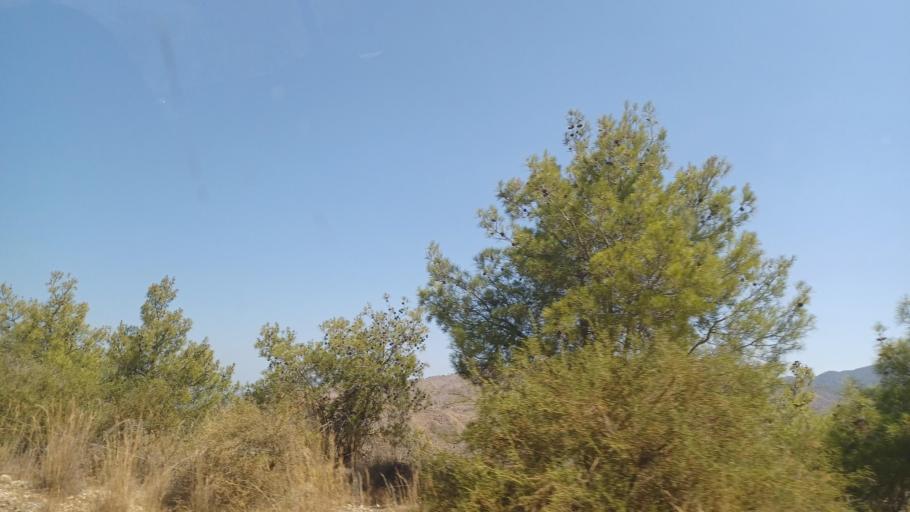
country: CY
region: Pafos
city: Polis
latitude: 35.0399
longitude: 32.4940
